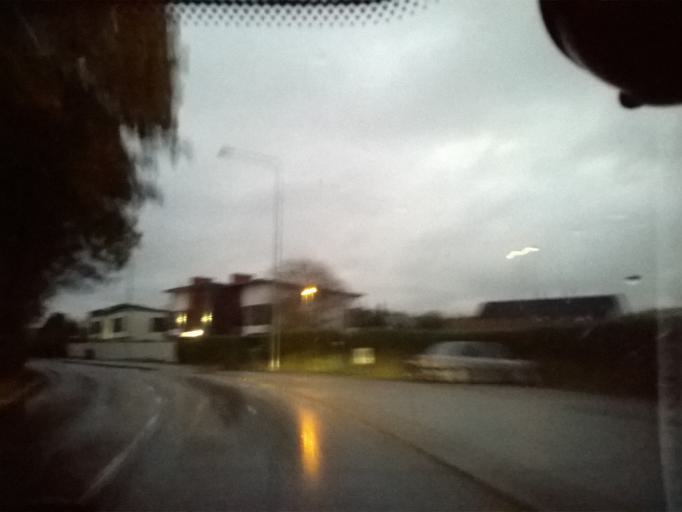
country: EE
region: Harju
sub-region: Viimsi vald
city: Haabneeme
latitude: 59.5170
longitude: 24.8203
